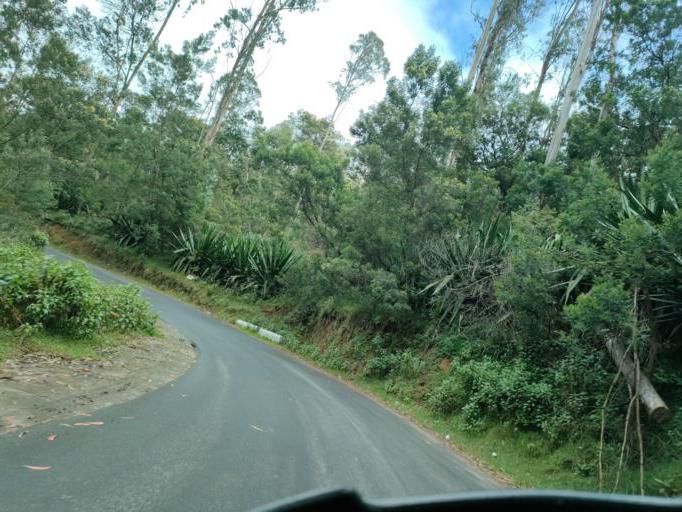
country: IN
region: Tamil Nadu
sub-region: Dindigul
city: Kodaikanal
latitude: 10.2433
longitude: 77.3702
